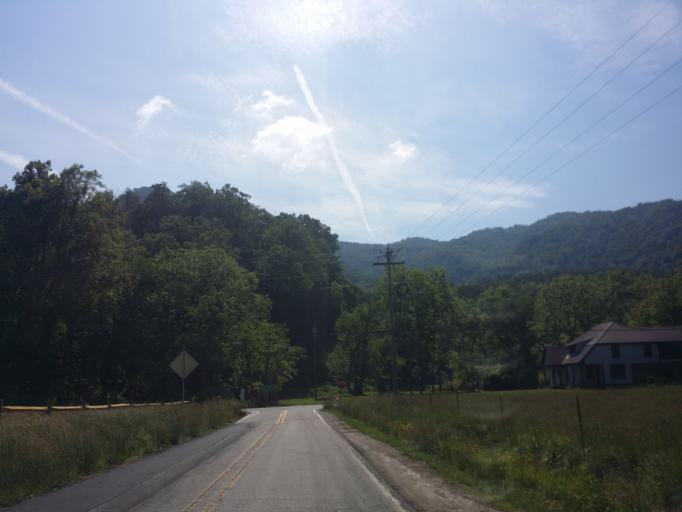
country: US
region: North Carolina
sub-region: Madison County
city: Marshall
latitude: 35.7733
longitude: -82.8743
